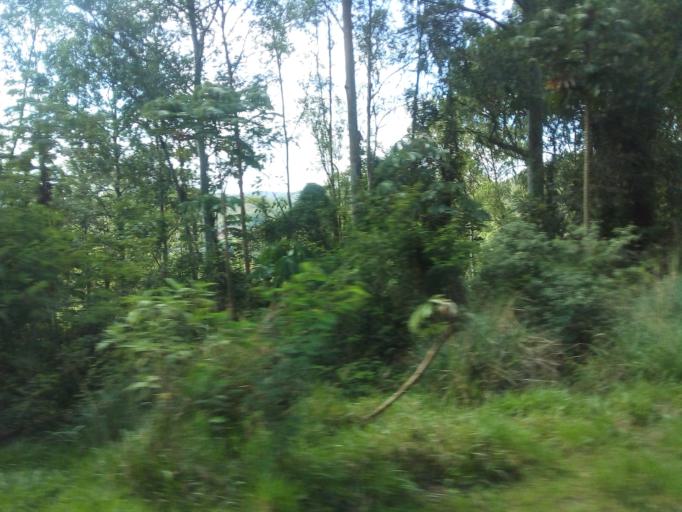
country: BR
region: Minas Gerais
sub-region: Raposos
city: Raposos
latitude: -19.8717
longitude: -43.7893
